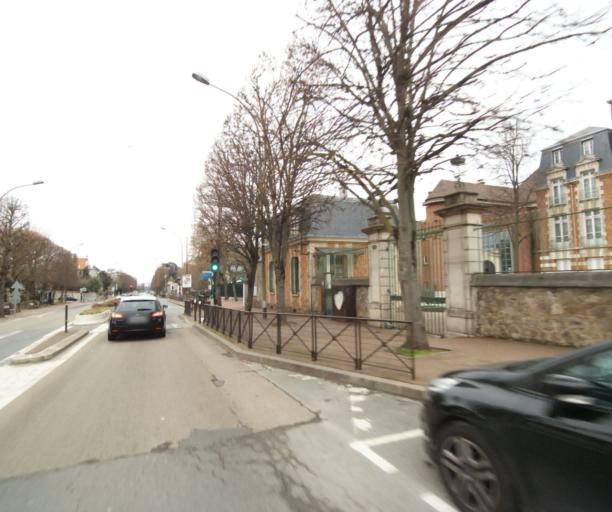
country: FR
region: Ile-de-France
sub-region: Departement des Hauts-de-Seine
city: Saint-Cloud
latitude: 48.8485
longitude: 2.2141
